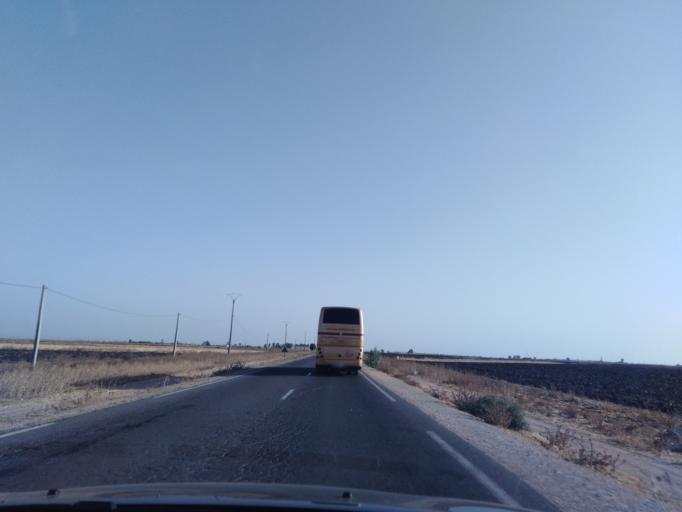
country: MA
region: Doukkala-Abda
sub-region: Safi
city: Youssoufia
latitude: 32.4839
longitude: -8.7681
